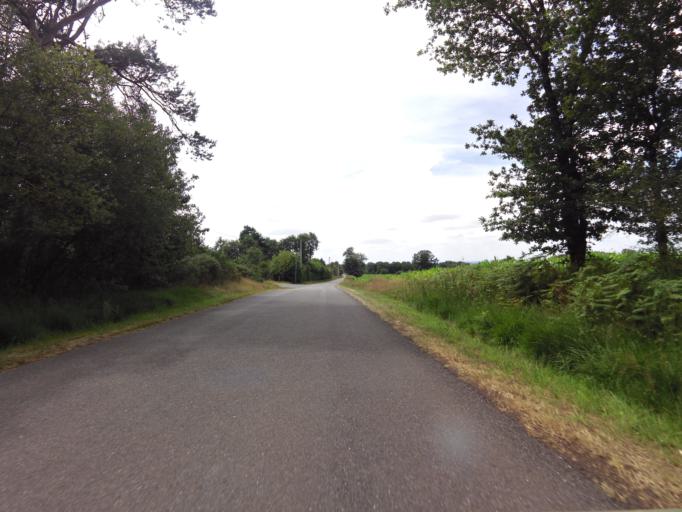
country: FR
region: Brittany
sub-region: Departement du Morbihan
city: Mauron
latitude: 48.0207
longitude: -2.2713
